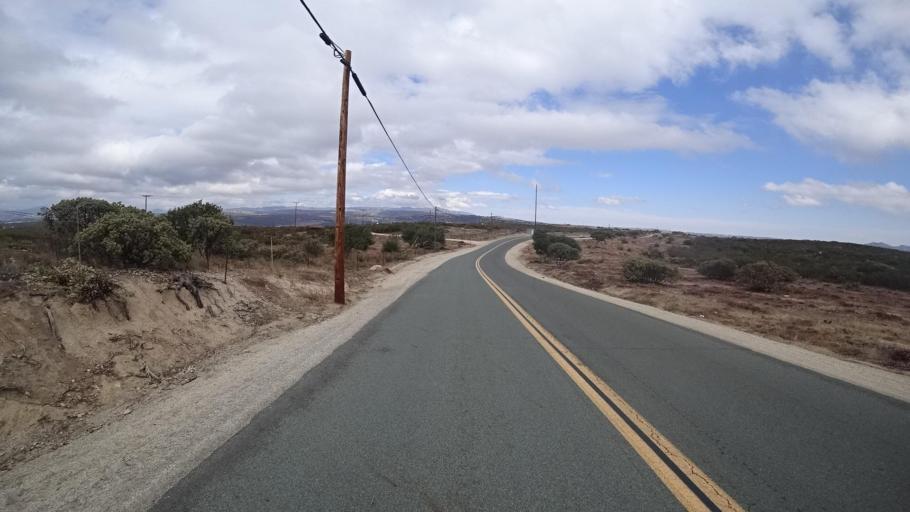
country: US
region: California
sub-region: San Diego County
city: Campo
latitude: 32.6495
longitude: -116.3169
